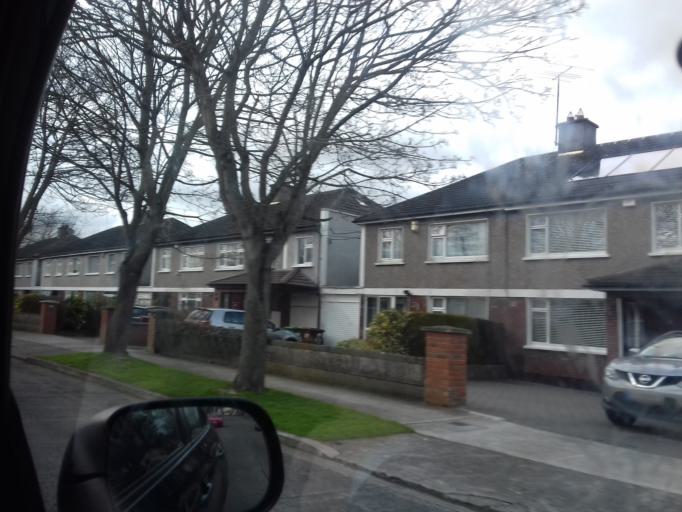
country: IE
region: Leinster
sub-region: Fingal County
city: Blanchardstown
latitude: 53.3861
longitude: -6.3901
